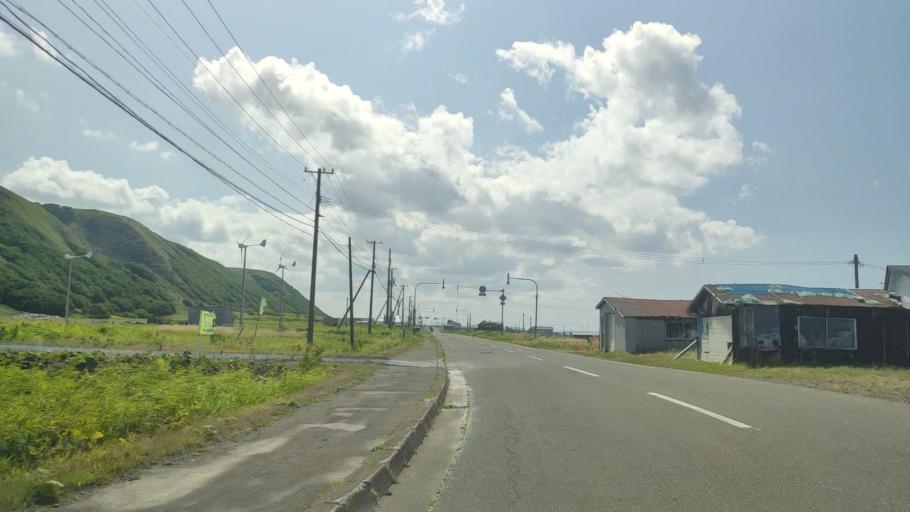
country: JP
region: Hokkaido
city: Wakkanai
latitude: 45.4131
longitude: 141.6357
